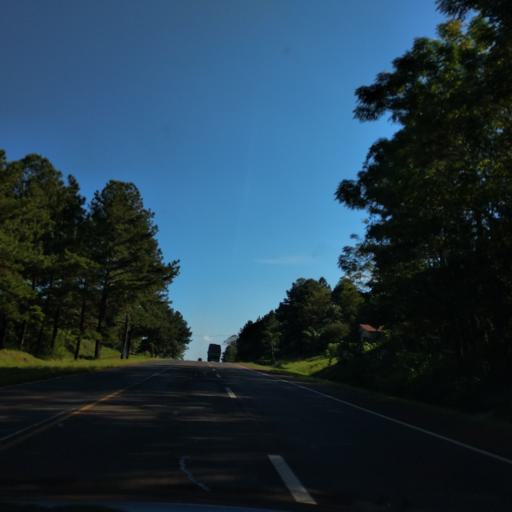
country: AR
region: Misiones
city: Jardin America
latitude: -27.0955
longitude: -55.3007
